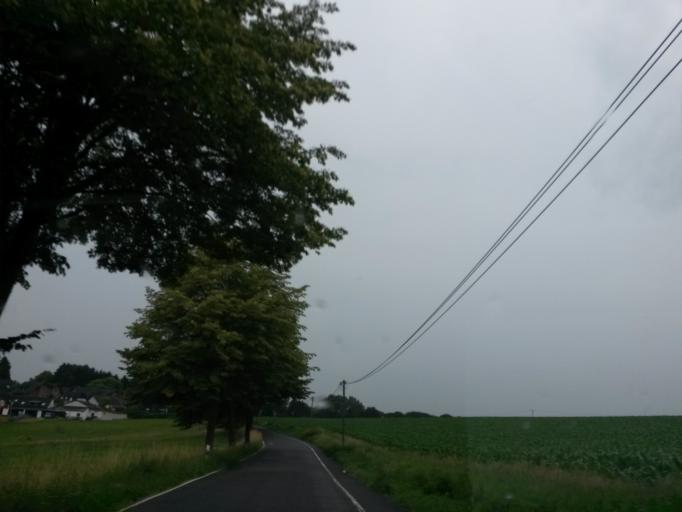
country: DE
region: North Rhine-Westphalia
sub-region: Regierungsbezirk Koln
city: Much
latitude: 50.9386
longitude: 7.3594
